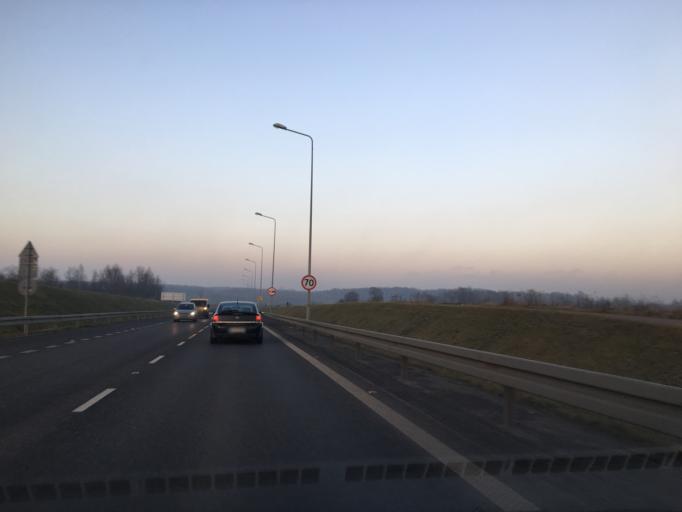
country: PL
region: Silesian Voivodeship
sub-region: Powiat tarnogorski
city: Radzionkow
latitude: 50.3618
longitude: 18.8694
